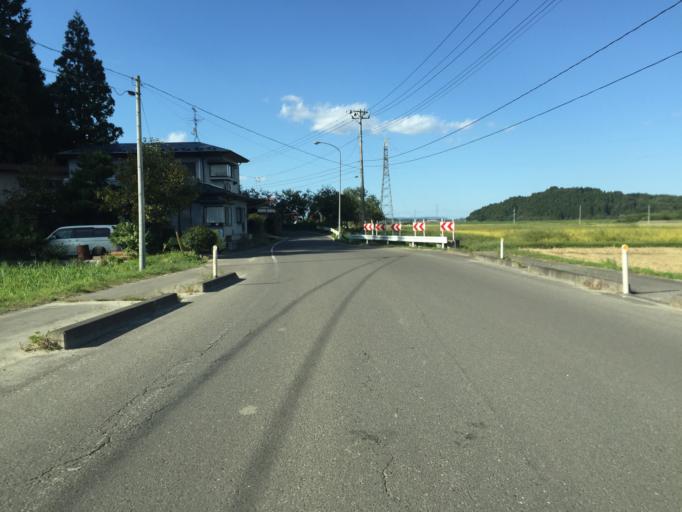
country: JP
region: Miyagi
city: Marumori
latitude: 37.8992
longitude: 140.7692
